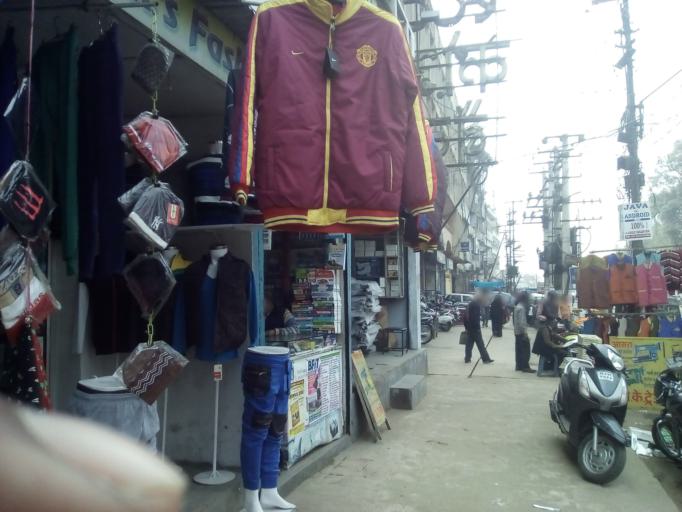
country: IN
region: Bihar
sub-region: Patna
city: Patna
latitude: 25.6189
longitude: 85.1507
